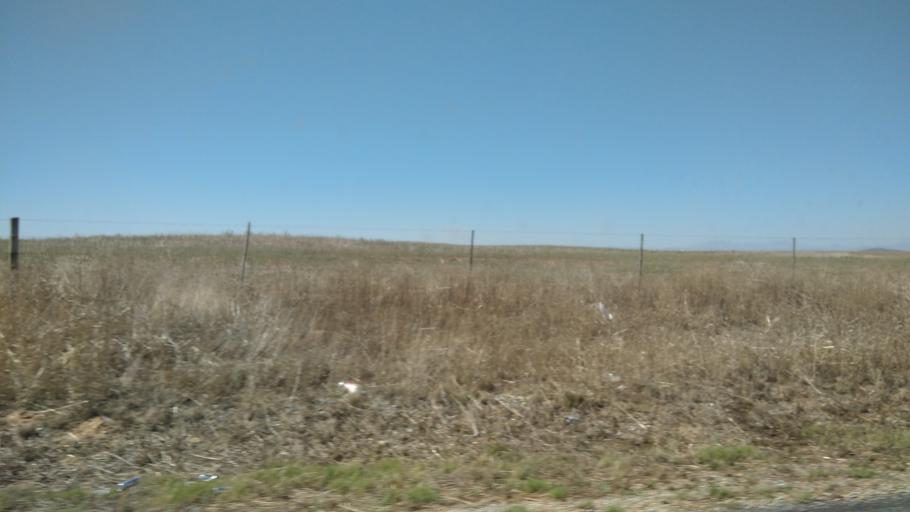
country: ZA
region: Western Cape
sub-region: West Coast District Municipality
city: Moorreesburg
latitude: -33.1822
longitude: 18.4947
